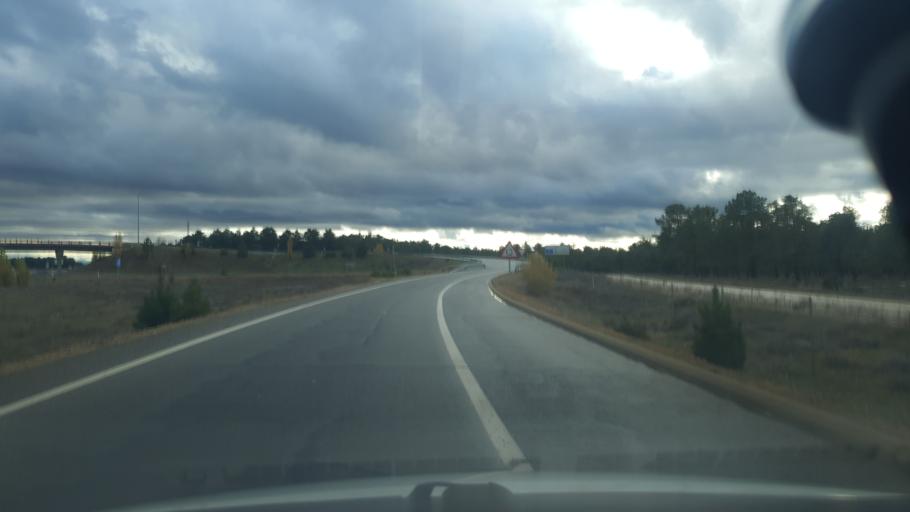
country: ES
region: Castille and Leon
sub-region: Provincia de Segovia
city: Sanchonuno
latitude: 41.2967
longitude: -4.3011
